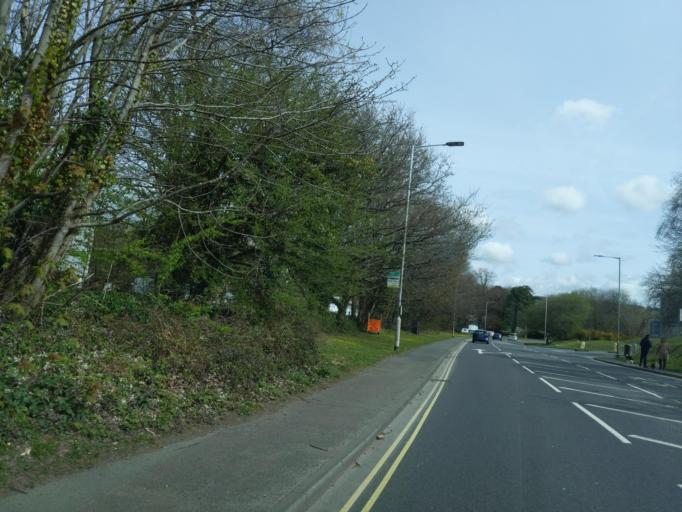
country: GB
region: England
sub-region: Devon
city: Plympton
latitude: 50.3965
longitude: -4.0446
